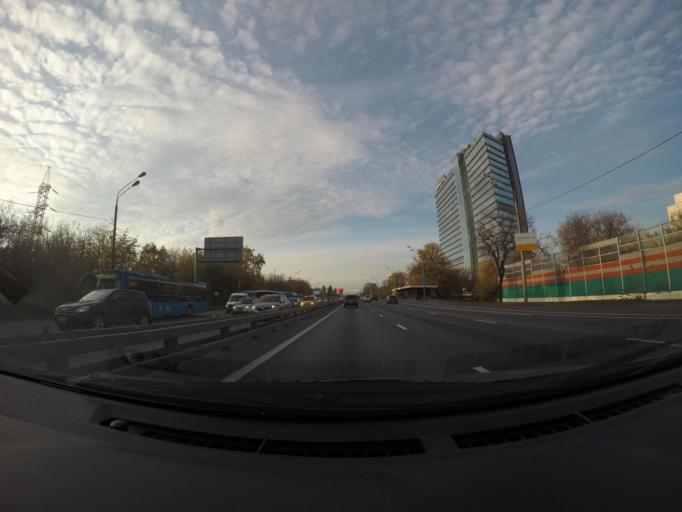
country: RU
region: Moscow
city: Khimki
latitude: 55.8936
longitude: 37.4302
